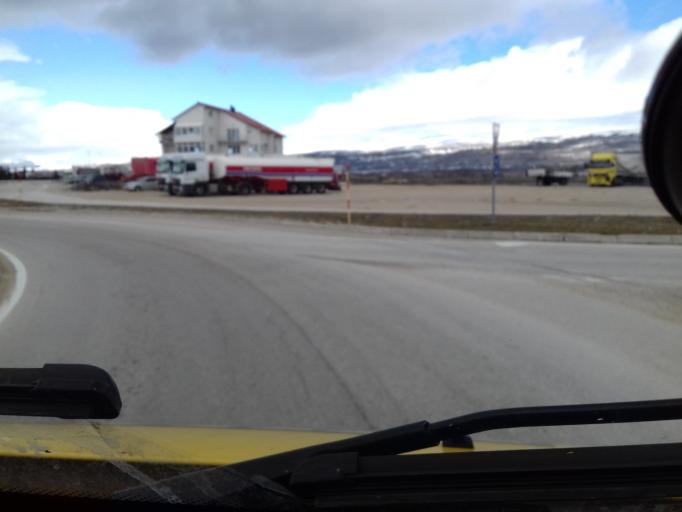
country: BA
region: Federation of Bosnia and Herzegovina
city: Tomislavgrad
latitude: 43.7138
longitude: 17.2396
